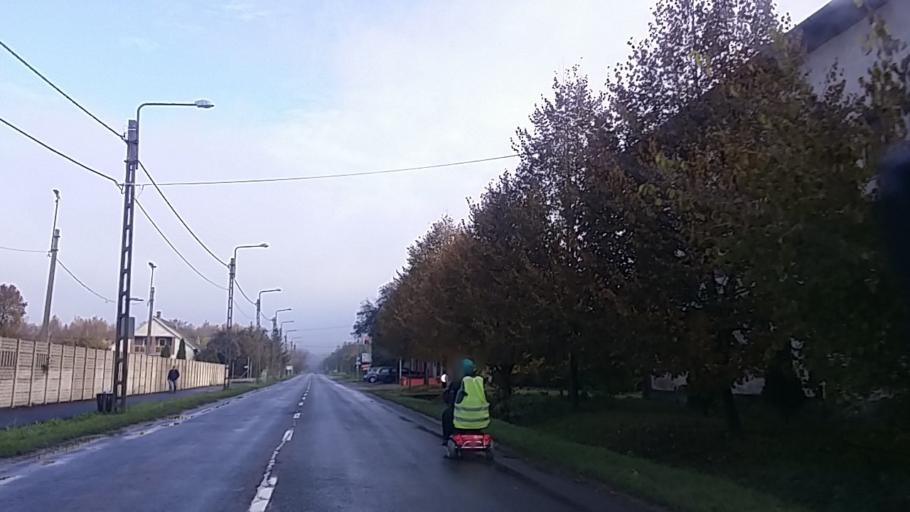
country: HU
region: Heves
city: Belapatfalva
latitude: 48.0607
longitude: 20.3535
